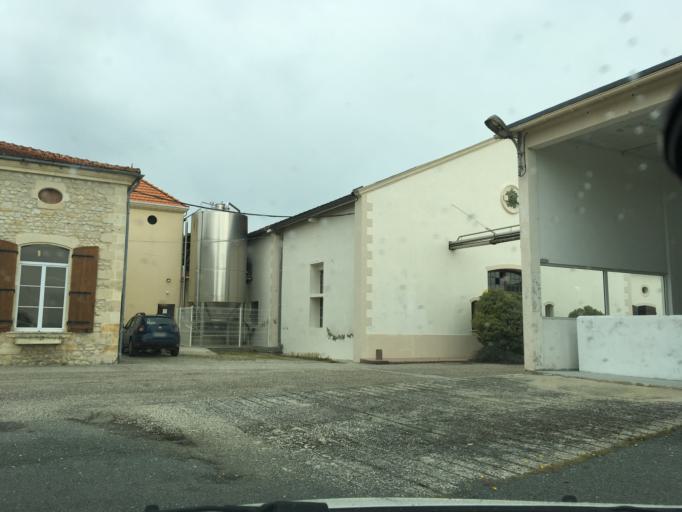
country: FR
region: Aquitaine
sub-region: Departement de la Gironde
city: Lesparre-Medoc
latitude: 45.3136
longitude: -0.8925
